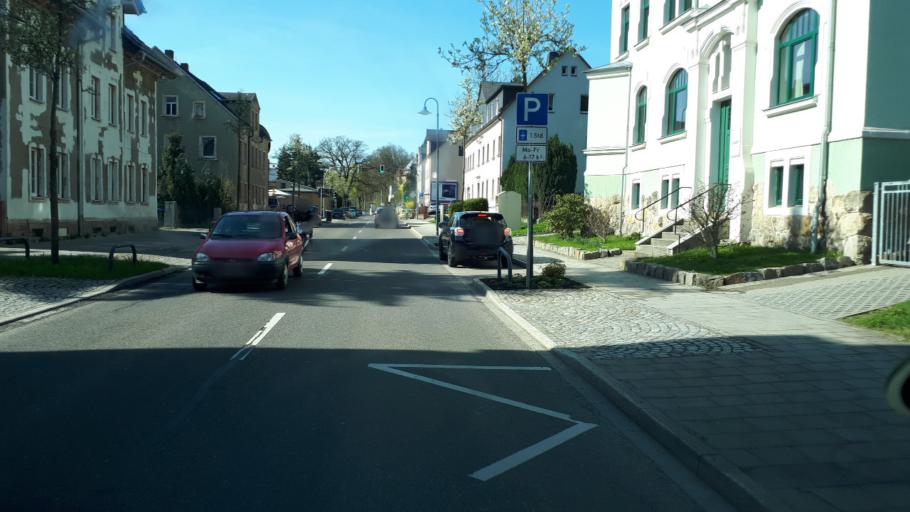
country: DE
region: Saxony
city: Chemnitz
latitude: 50.7871
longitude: 12.9515
